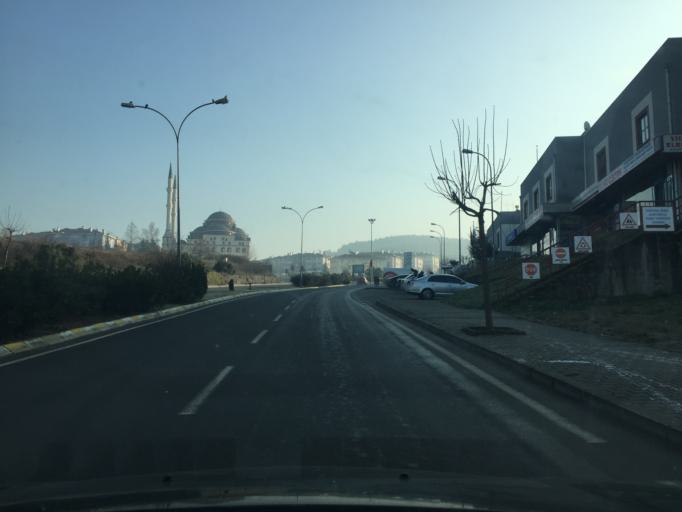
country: TR
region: Duzce
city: Duzce
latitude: 40.8682
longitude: 31.2249
